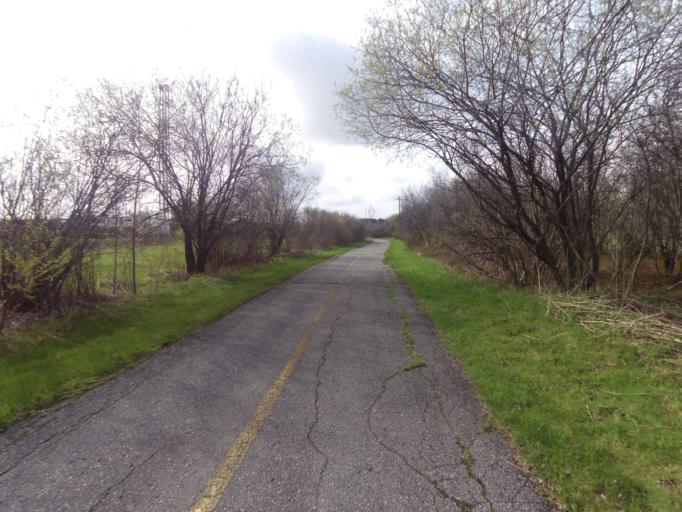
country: CA
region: Ontario
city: Ottawa
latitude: 45.3338
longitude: -75.7310
